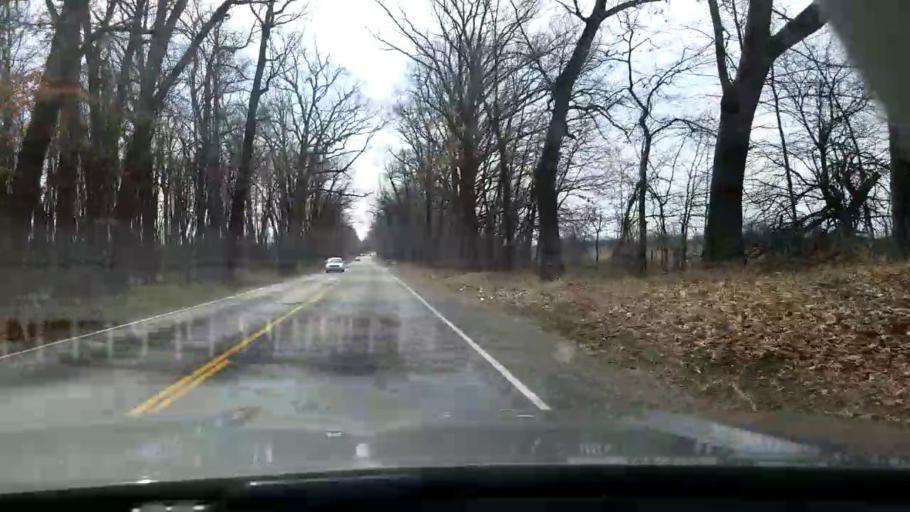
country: US
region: Michigan
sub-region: Jackson County
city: Spring Arbor
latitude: 42.1747
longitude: -84.5202
